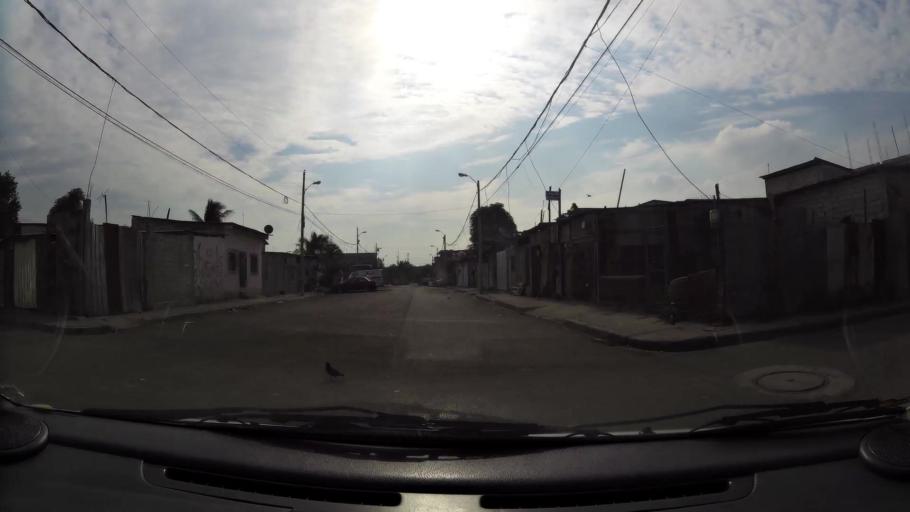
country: EC
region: Guayas
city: Guayaquil
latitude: -2.2477
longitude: -79.9076
